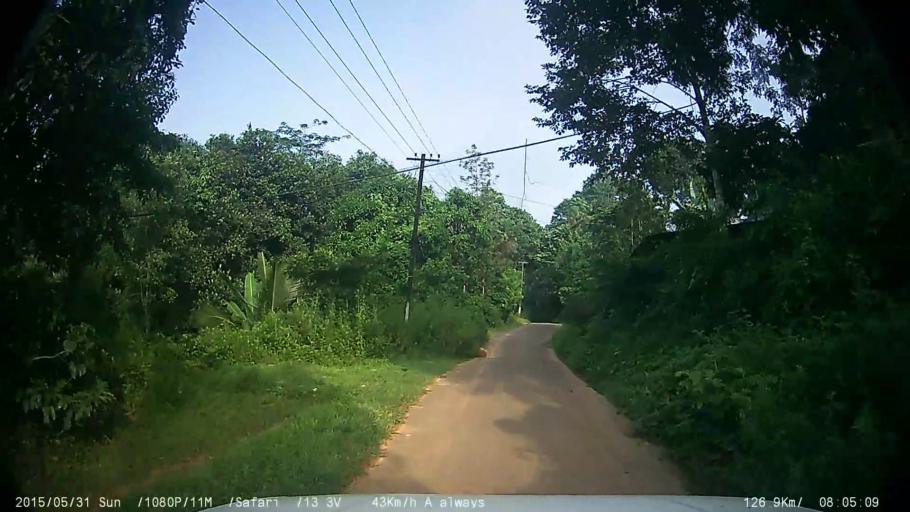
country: IN
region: Kerala
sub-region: Wayanad
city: Kalpetta
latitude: 11.6352
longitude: 76.0359
